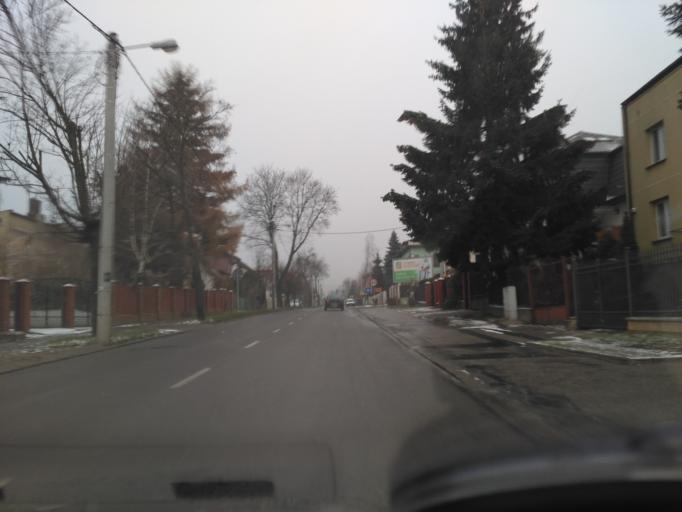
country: PL
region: Lublin Voivodeship
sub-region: Powiat lubelski
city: Lublin
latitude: 51.2250
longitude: 22.5863
